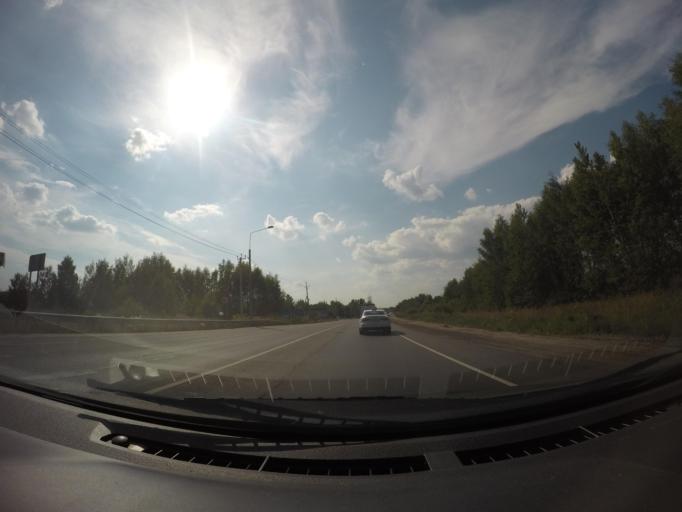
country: RU
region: Moskovskaya
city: Kratovo
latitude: 55.6398
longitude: 38.1729
